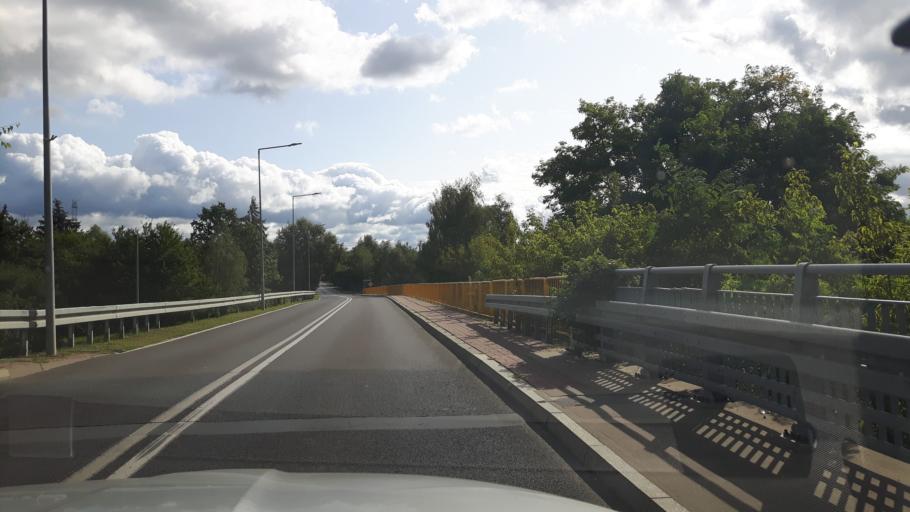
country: PL
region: Masovian Voivodeship
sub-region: Powiat legionowski
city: Stanislawow Pierwszy
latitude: 52.3971
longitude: 21.0417
